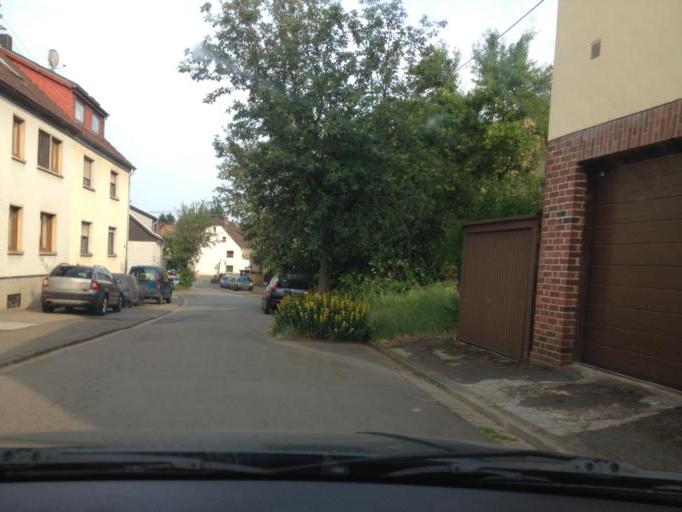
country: DE
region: Saarland
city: Ottweiler
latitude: 49.4318
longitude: 7.1577
